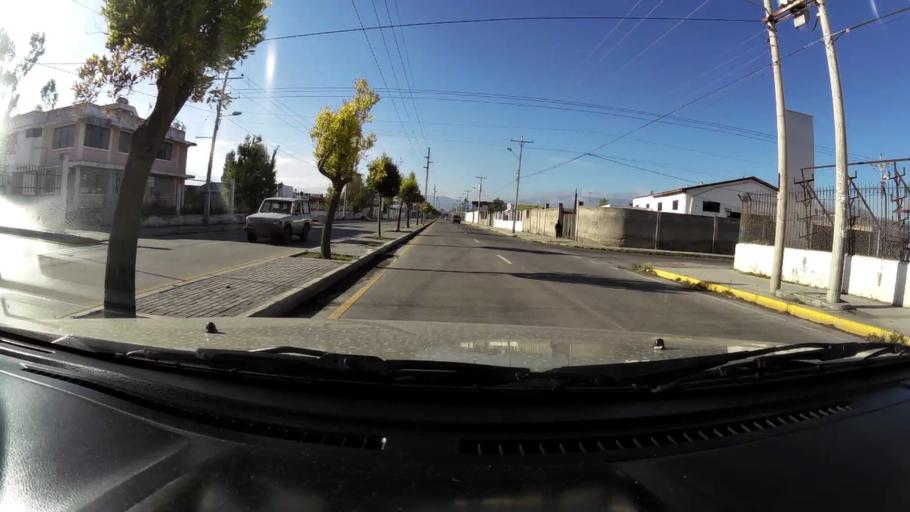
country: EC
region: Chimborazo
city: Riobamba
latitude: -1.6821
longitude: -78.6301
